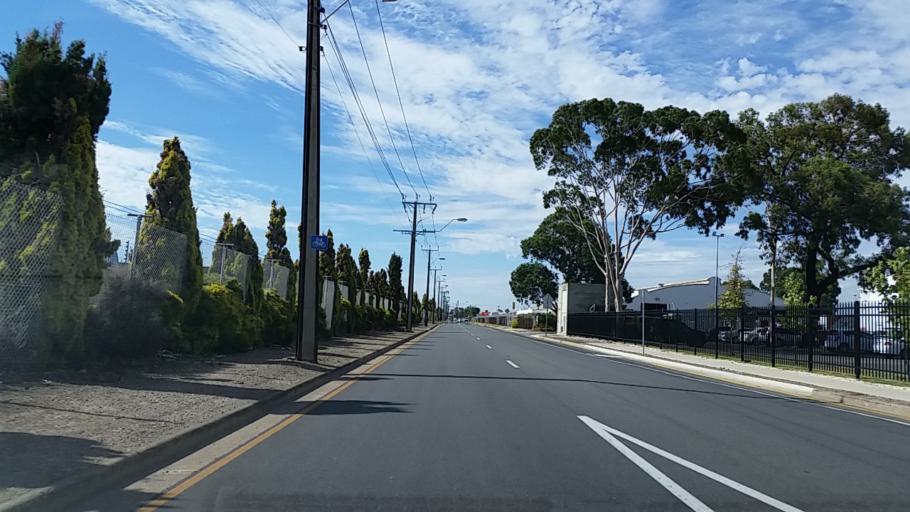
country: AU
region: South Australia
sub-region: Charles Sturt
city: Woodville North
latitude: -34.8595
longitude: 138.5384
